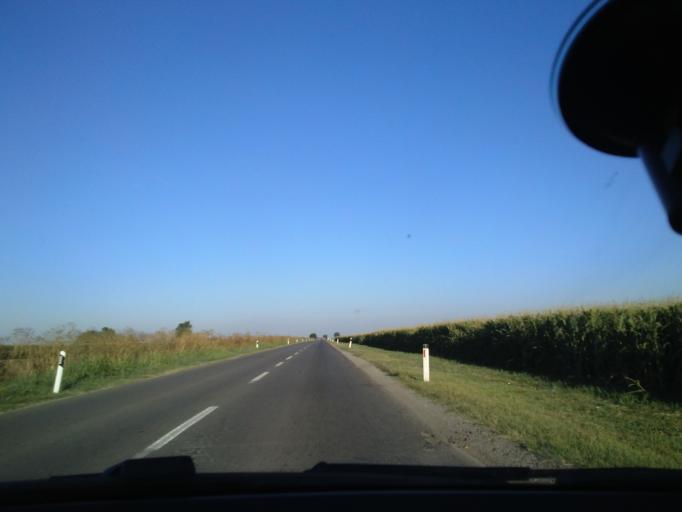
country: RS
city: Maglic
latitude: 45.3898
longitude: 19.4882
